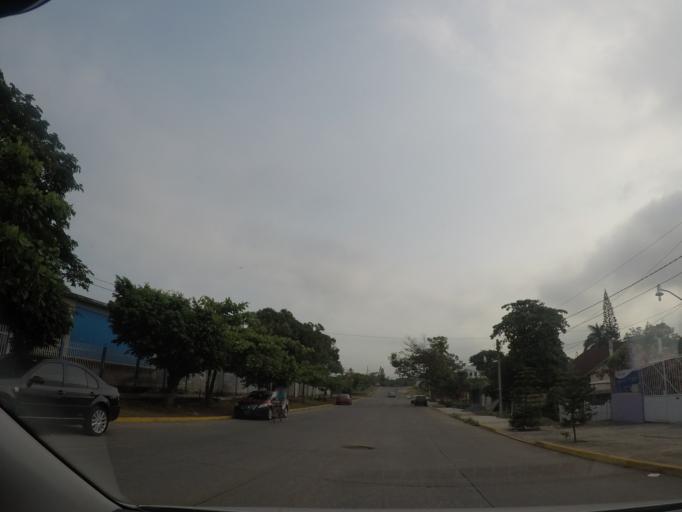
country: MX
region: Oaxaca
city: Matias Romero
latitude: 16.8735
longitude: -95.0467
